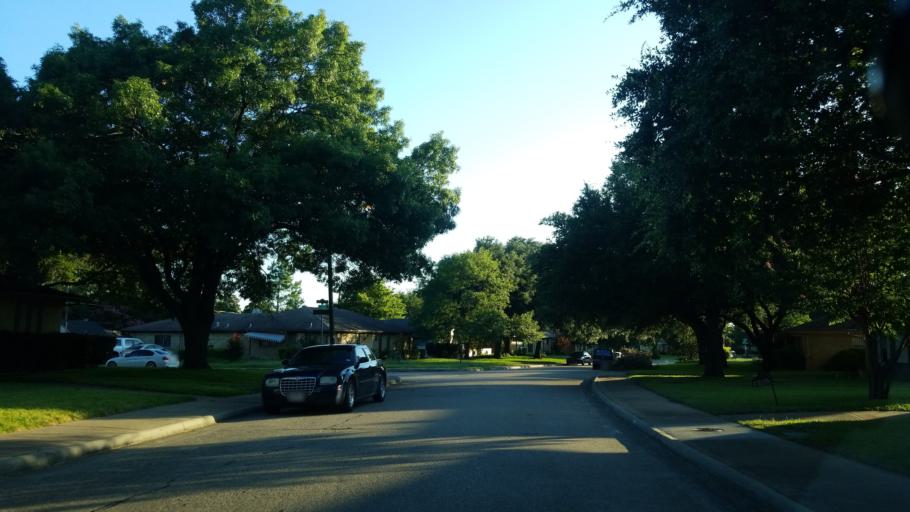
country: US
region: Texas
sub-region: Dallas County
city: Balch Springs
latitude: 32.7903
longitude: -96.6945
